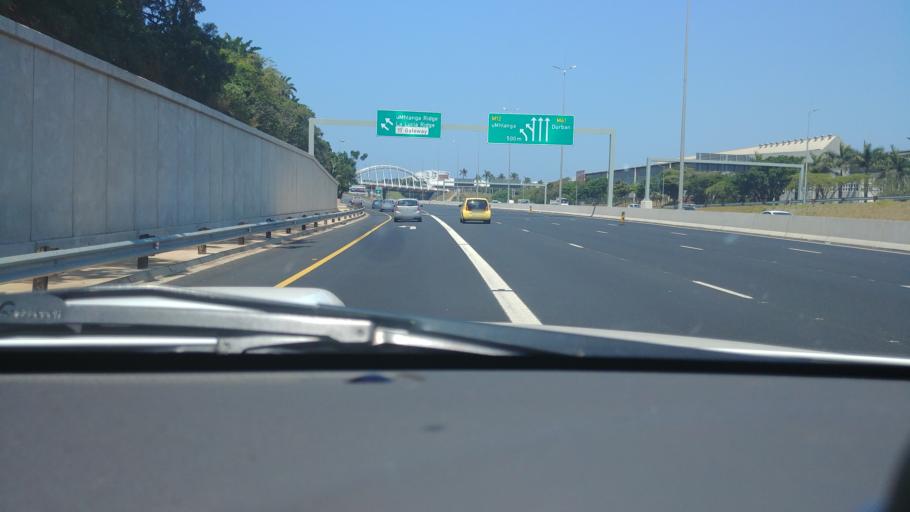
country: ZA
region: KwaZulu-Natal
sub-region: eThekwini Metropolitan Municipality
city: Durban
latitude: -29.7247
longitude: 31.0600
